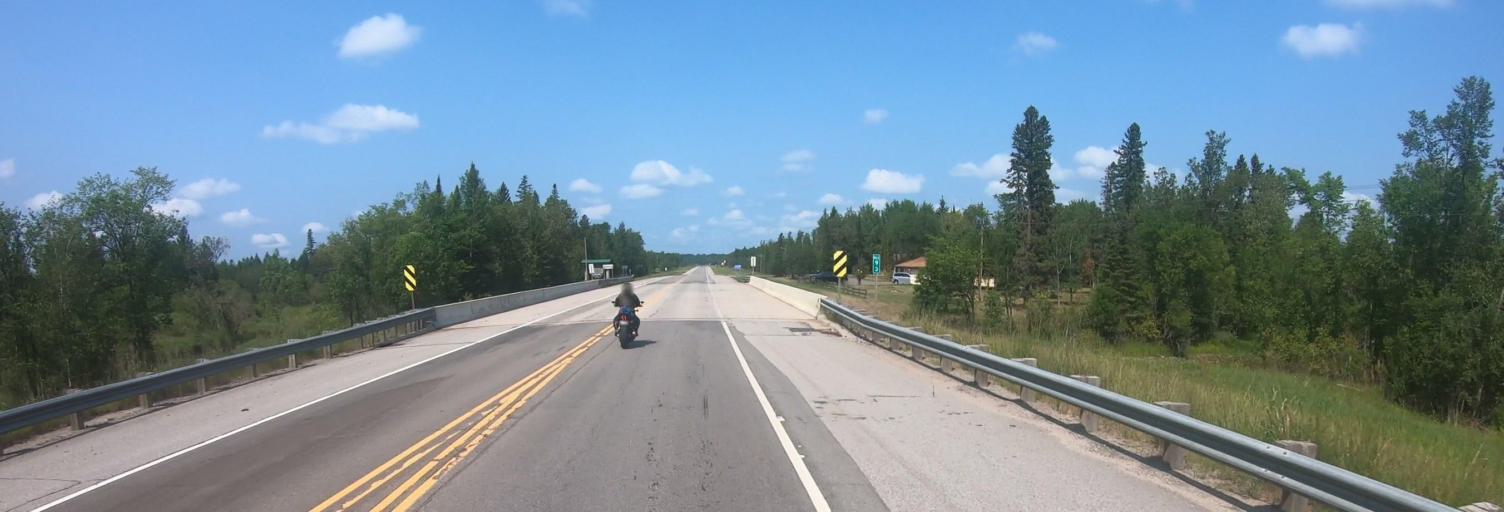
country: US
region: Minnesota
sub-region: Saint Louis County
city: Mountain Iron
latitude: 47.8540
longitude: -92.6983
